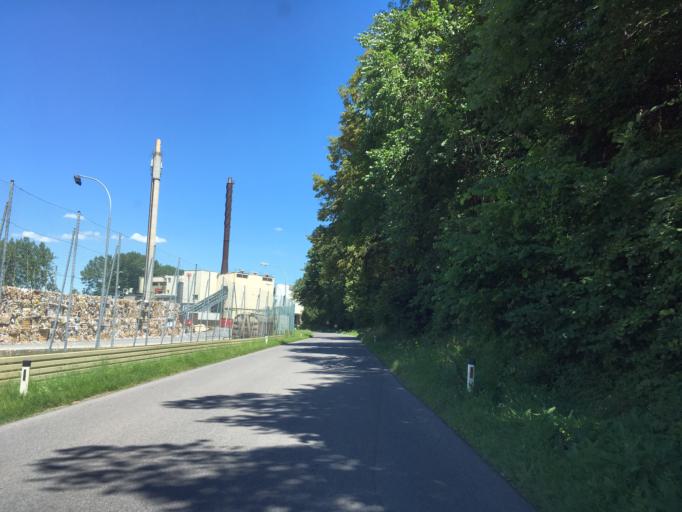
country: AT
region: Lower Austria
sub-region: Politischer Bezirk Neunkirchen
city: Pitten
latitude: 47.7039
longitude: 16.1725
